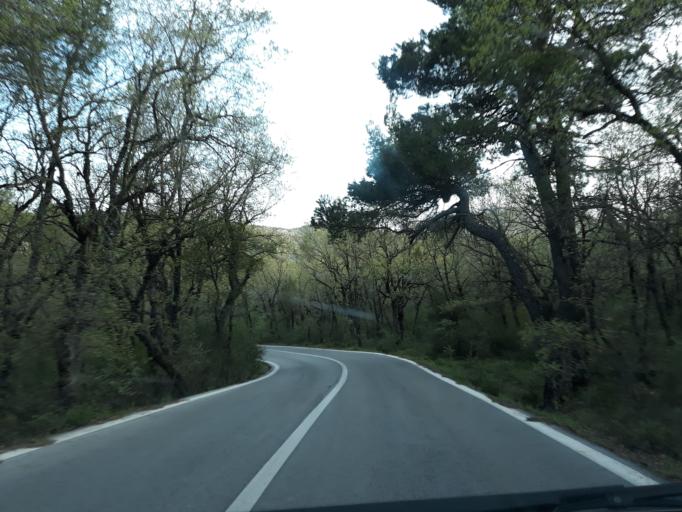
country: GR
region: Attica
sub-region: Nomarchia Anatolikis Attikis
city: Afidnes
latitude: 38.1968
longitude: 23.7840
